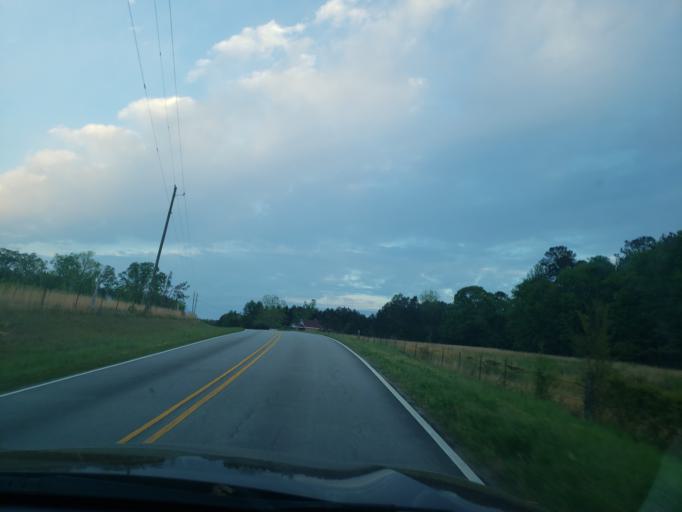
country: US
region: Alabama
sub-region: Tallapoosa County
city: Camp Hill
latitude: 32.7017
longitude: -85.6968
